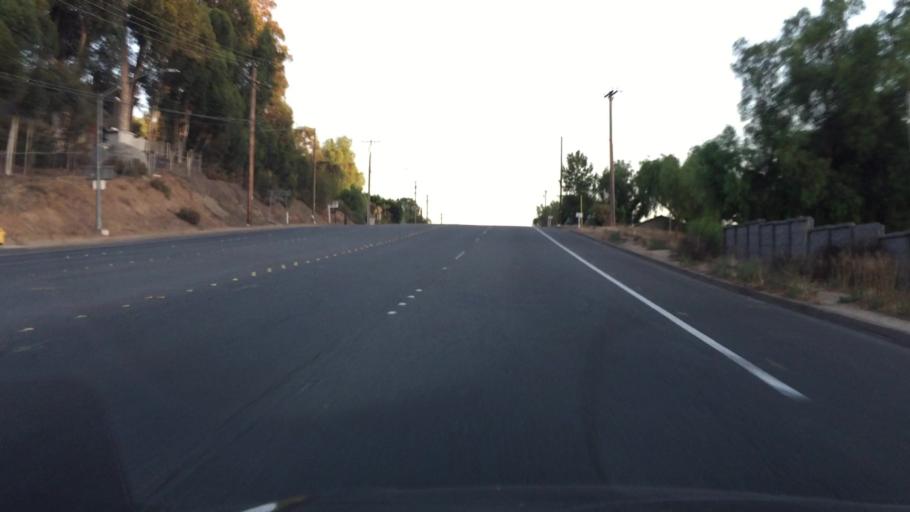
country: US
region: California
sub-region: San Diego County
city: Bostonia
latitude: 32.7781
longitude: -116.9280
